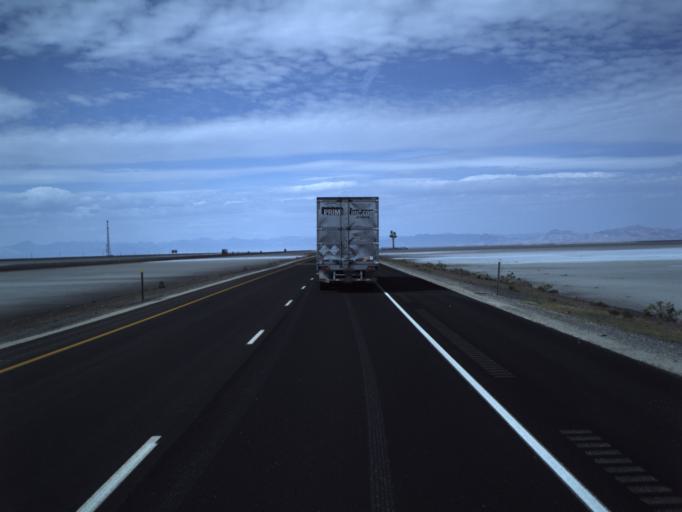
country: US
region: Utah
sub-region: Tooele County
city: Wendover
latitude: 40.7327
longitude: -113.5374
